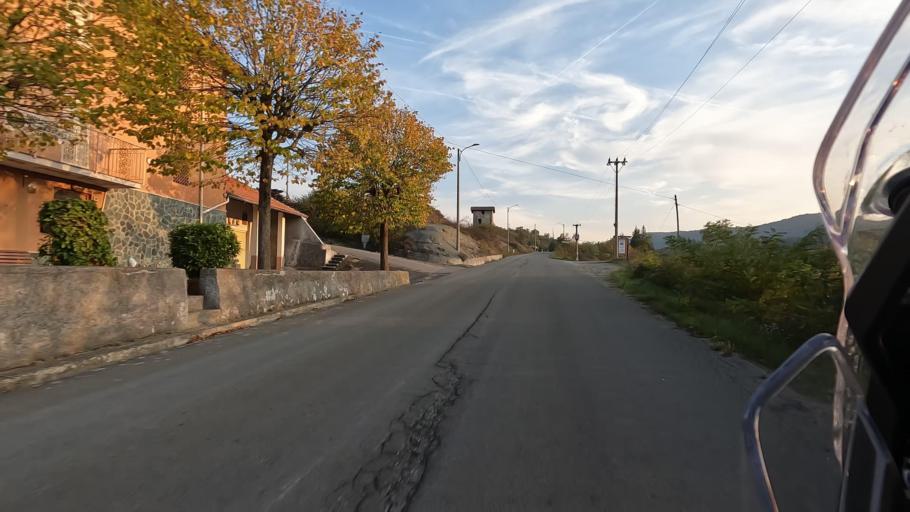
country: IT
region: Liguria
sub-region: Provincia di Savona
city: Mioglia
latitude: 44.4844
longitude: 8.4128
